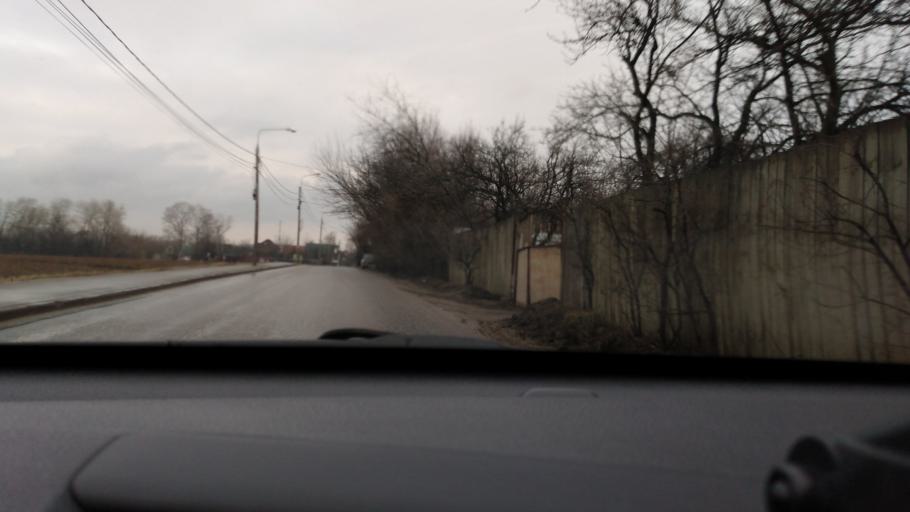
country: RU
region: Moscow
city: Zagor'ye
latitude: 55.5609
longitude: 37.6650
